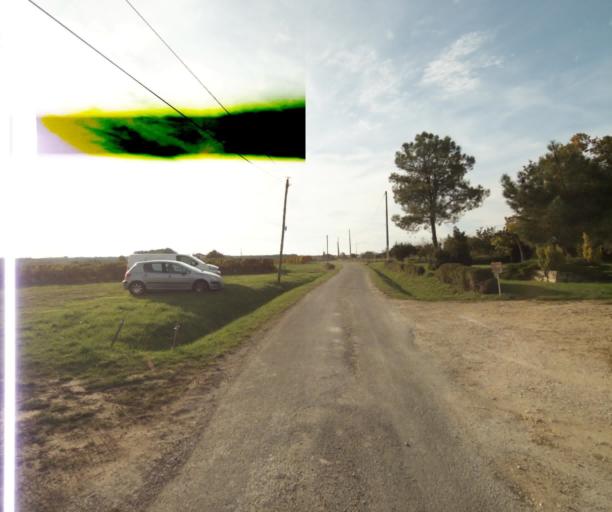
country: FR
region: Midi-Pyrenees
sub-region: Departement du Tarn-et-Garonne
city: Campsas
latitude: 43.8809
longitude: 1.3439
